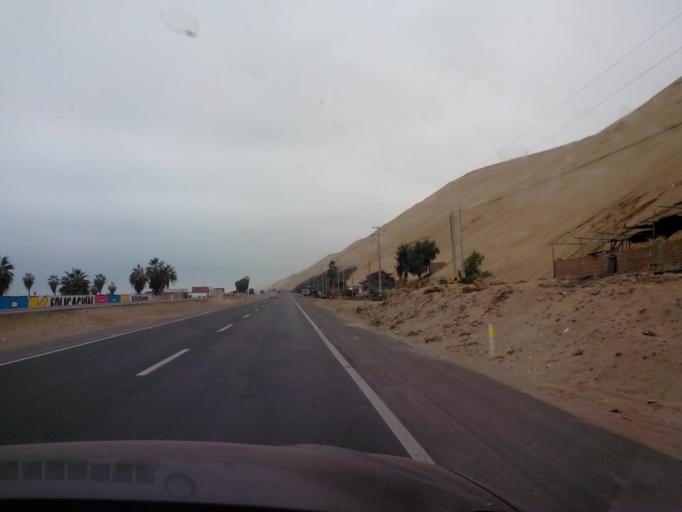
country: PE
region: Ica
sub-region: Provincia de Chincha
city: San Pedro
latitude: -13.3495
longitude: -76.2242
